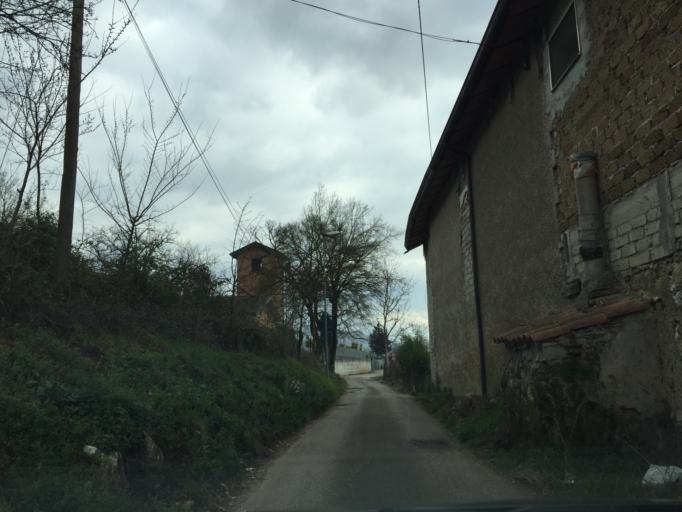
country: IT
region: Latium
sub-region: Provincia di Frosinone
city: Cassino
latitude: 41.4823
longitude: 13.8038
